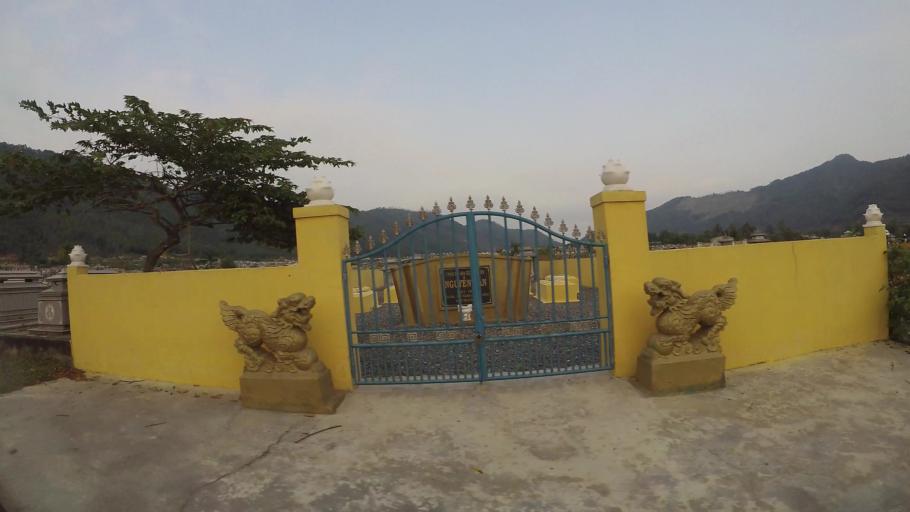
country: VN
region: Da Nang
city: Lien Chieu
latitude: 16.0591
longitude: 108.1127
